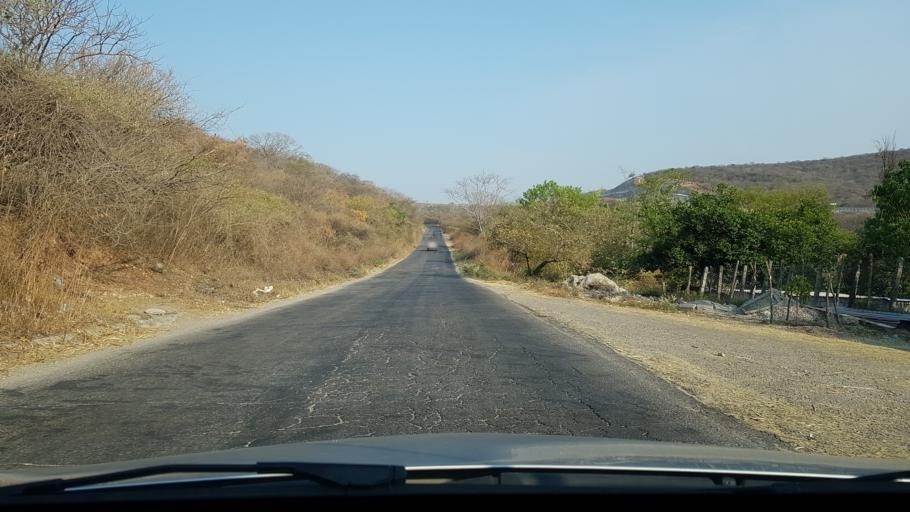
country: MX
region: Morelos
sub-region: Tepalcingo
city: Zacapalco
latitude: 18.6552
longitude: -99.0379
